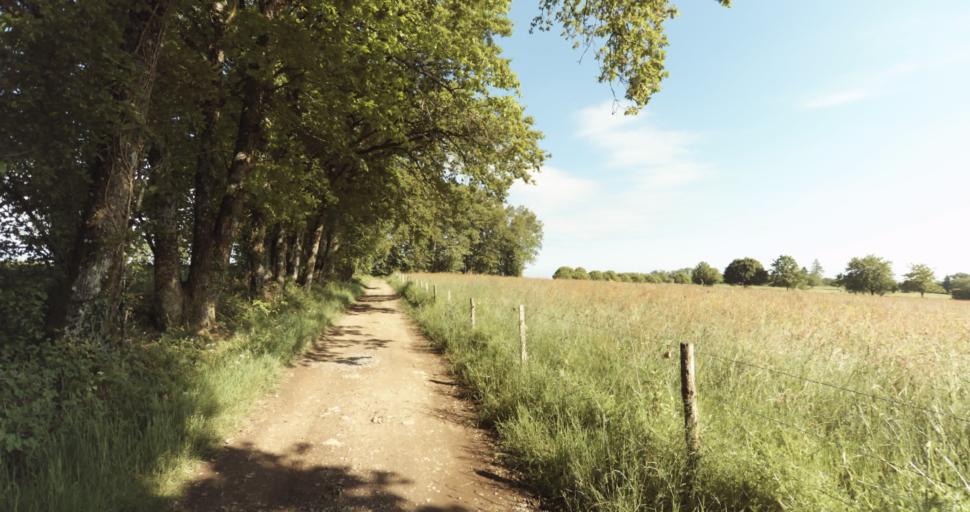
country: FR
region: Limousin
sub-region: Departement de la Haute-Vienne
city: Solignac
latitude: 45.7207
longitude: 1.2442
